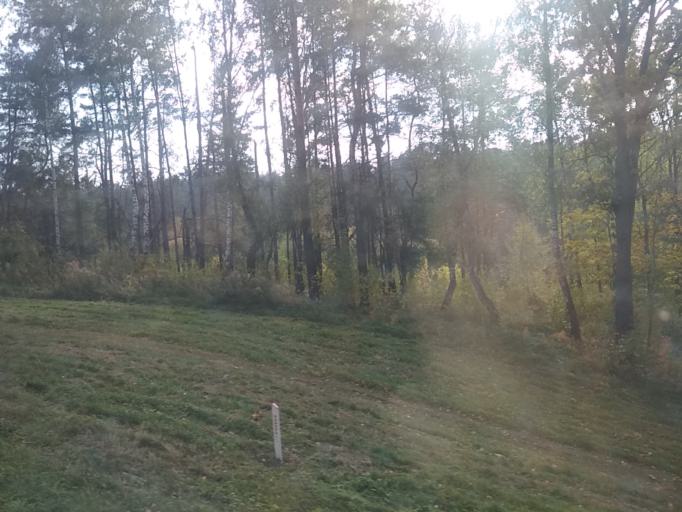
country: BY
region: Minsk
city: Machulishchy
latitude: 53.7855
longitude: 27.6018
